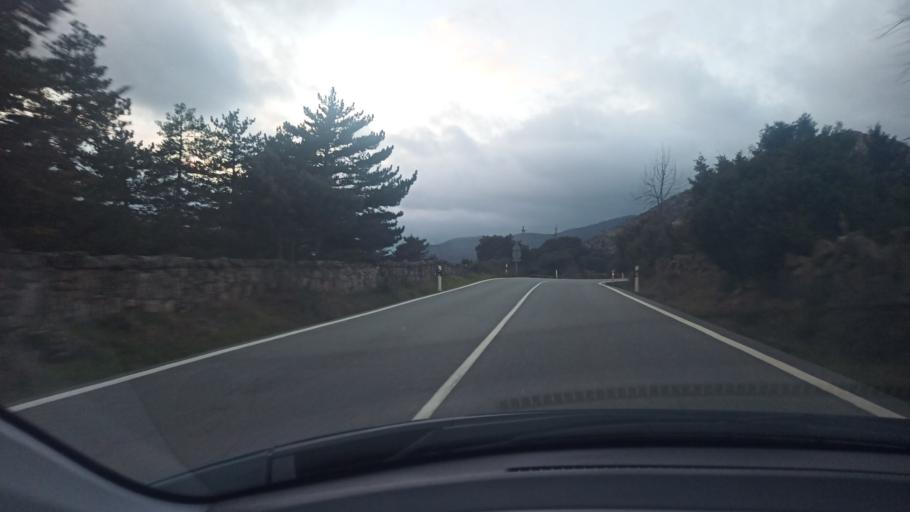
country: ES
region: Madrid
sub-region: Provincia de Madrid
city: El Escorial
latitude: 40.5391
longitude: -4.1378
